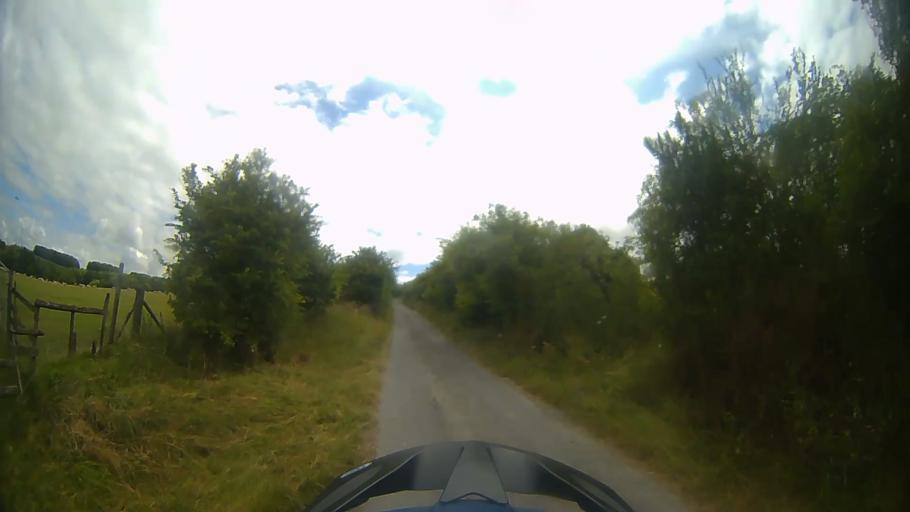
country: GB
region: England
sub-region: Oxfordshire
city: Wantage
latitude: 51.5635
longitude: -1.4462
